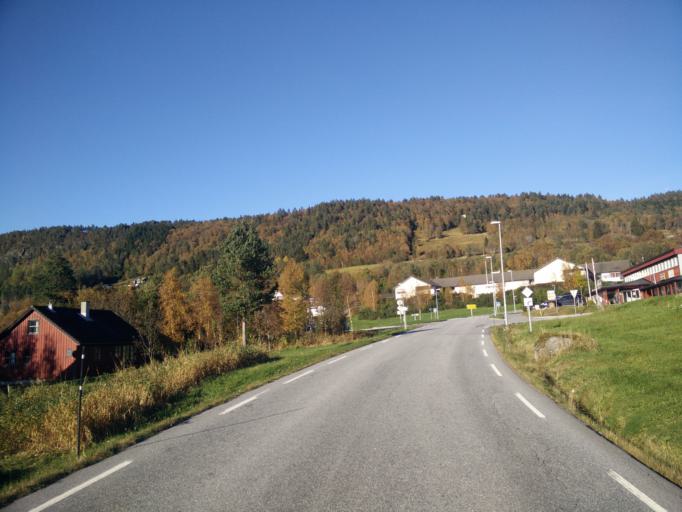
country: NO
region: More og Romsdal
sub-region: Halsa
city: Liaboen
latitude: 63.1183
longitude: 8.3078
